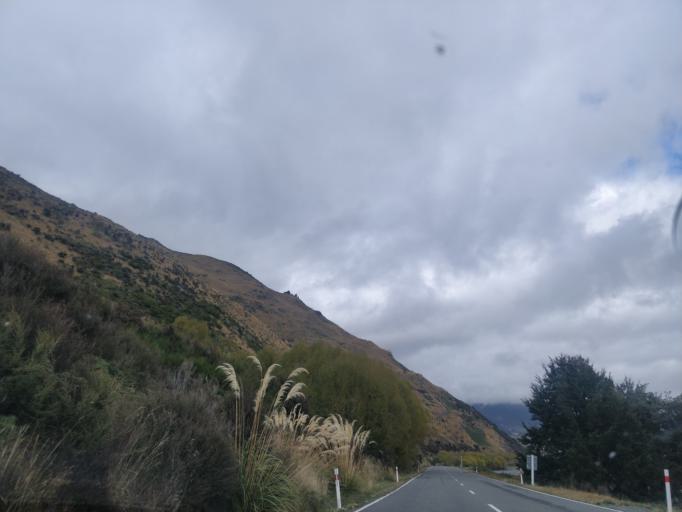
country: NZ
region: Canterbury
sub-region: Waimakariri District
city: Oxford
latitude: -43.0091
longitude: 171.7264
